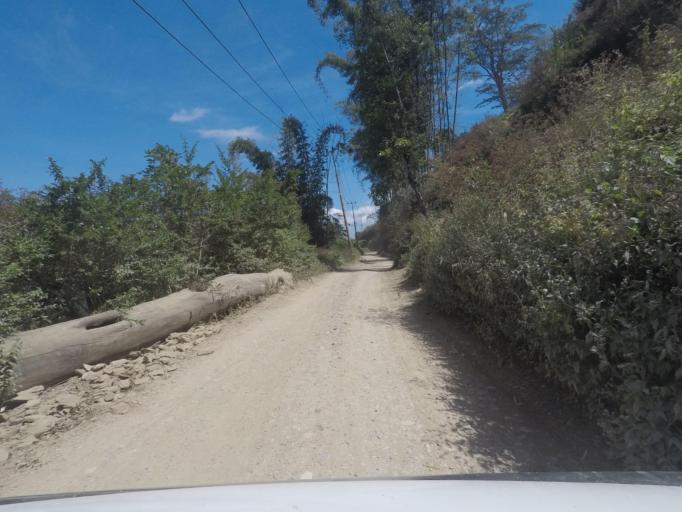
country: TL
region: Ermera
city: Gleno
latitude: -8.7525
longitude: 125.3310
